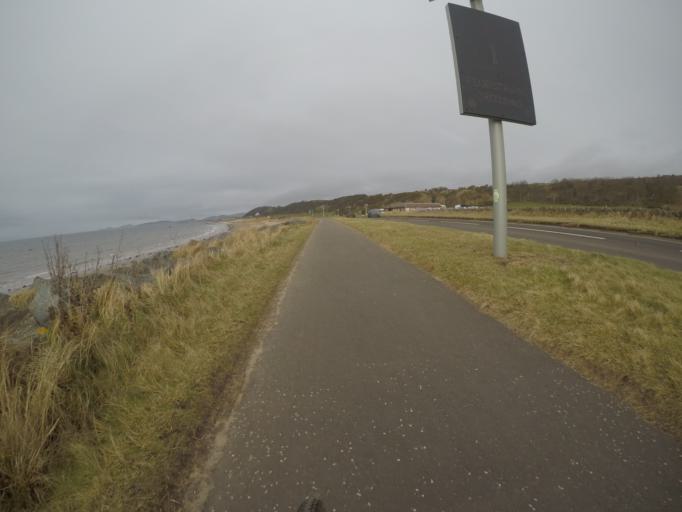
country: GB
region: Scotland
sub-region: North Ayrshire
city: Ardrossan
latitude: 55.6599
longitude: -4.8309
